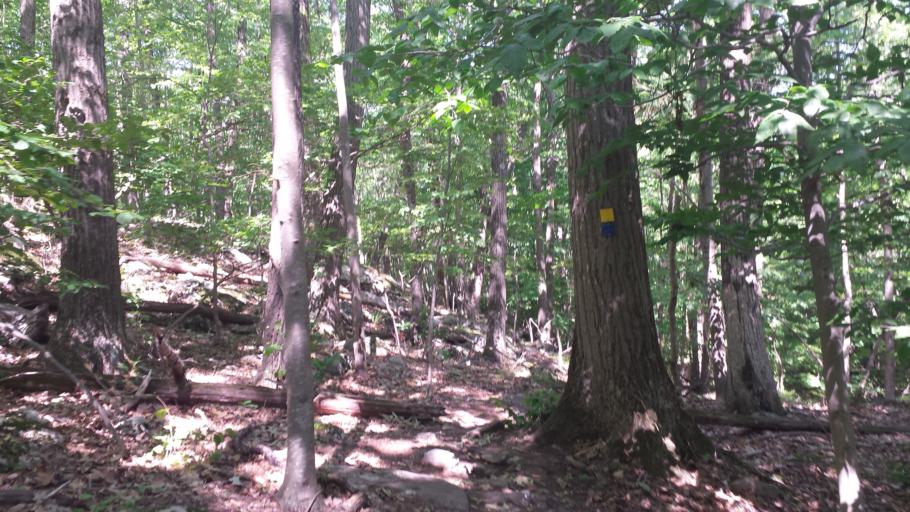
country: US
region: New York
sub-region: Putnam County
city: Peach Lake
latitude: 41.3152
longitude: -73.5532
